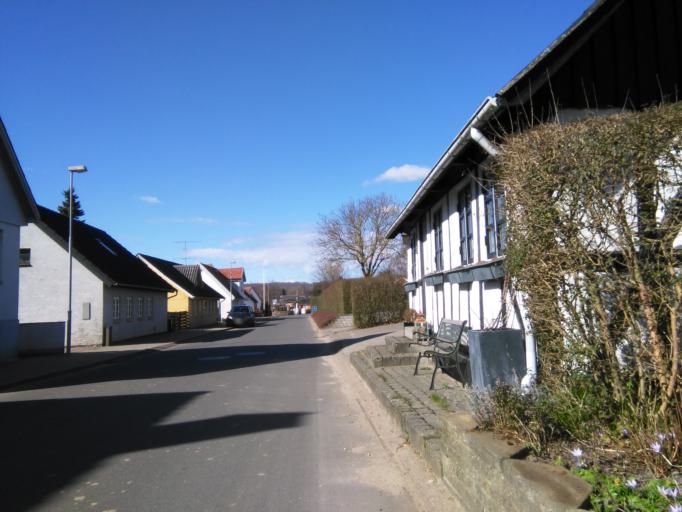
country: DK
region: Central Jutland
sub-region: Horsens Kommune
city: Horsens
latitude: 55.8914
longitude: 10.0065
